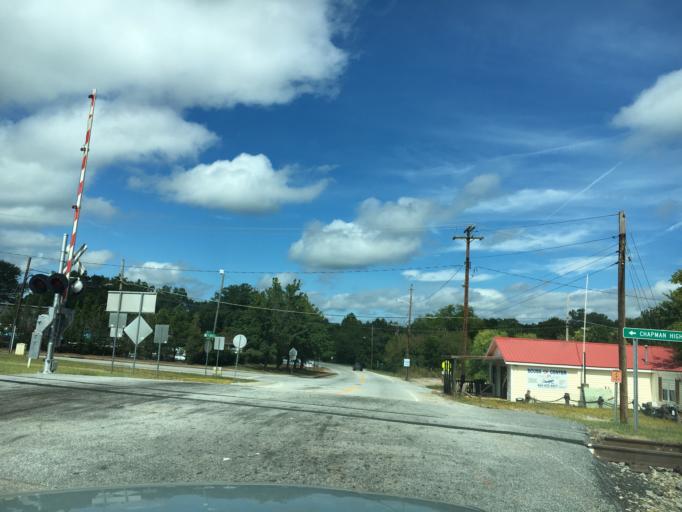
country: US
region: South Carolina
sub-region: Spartanburg County
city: Inman
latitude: 35.0486
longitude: -82.0907
